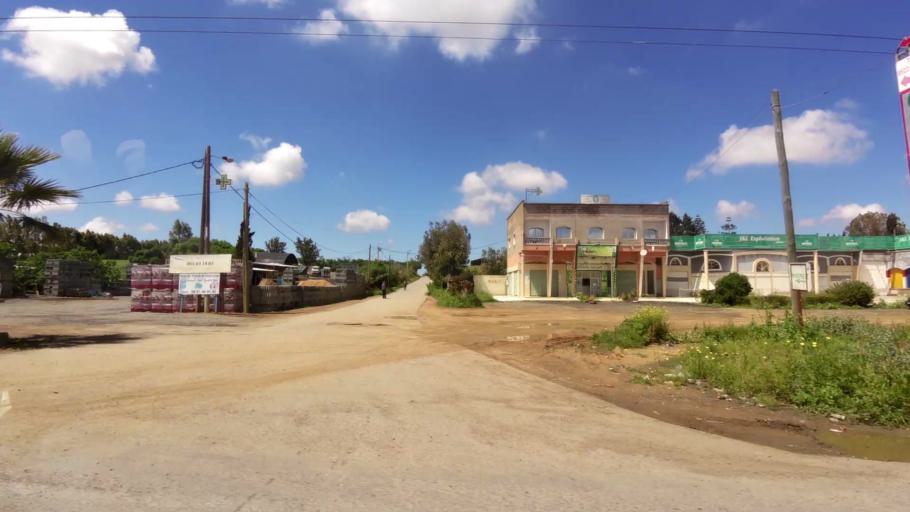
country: MA
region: Grand Casablanca
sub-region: Nouaceur
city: Dar Bouazza
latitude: 33.4368
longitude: -7.8266
